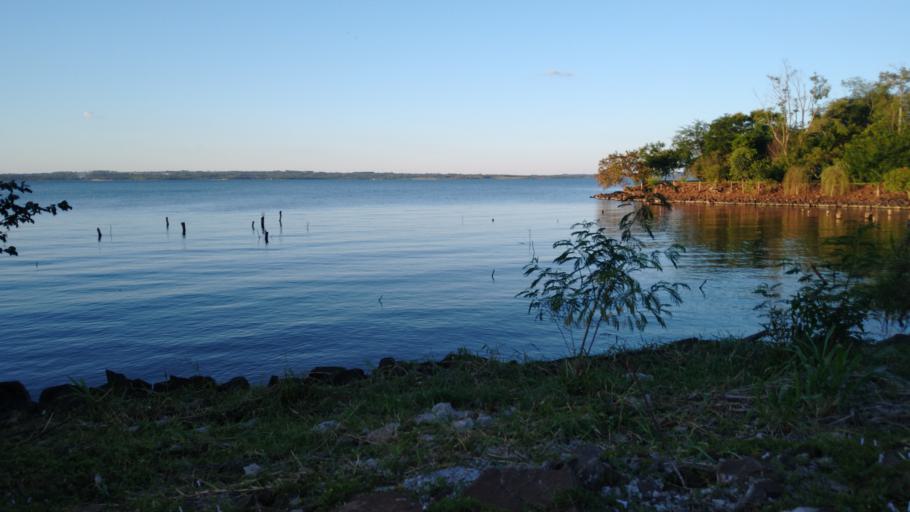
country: AR
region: Misiones
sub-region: Departamento de Capital
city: Posadas
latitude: -27.3545
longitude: -55.9384
